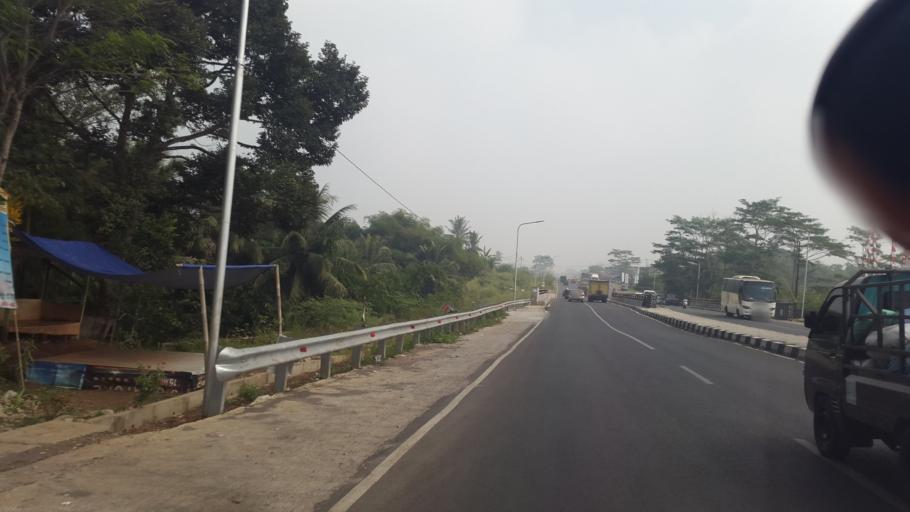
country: ID
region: West Java
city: Sukabumi
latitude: -6.9323
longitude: 106.9021
